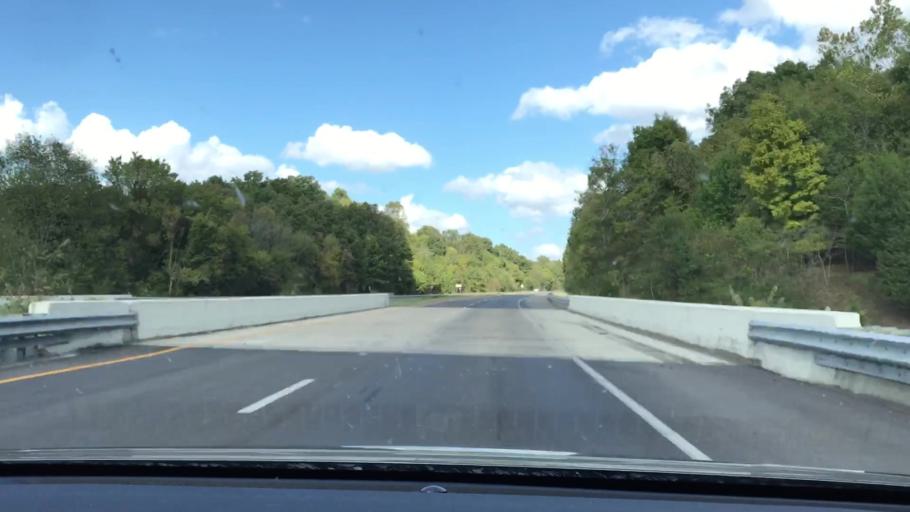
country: US
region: Kentucky
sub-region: Marshall County
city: Benton
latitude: 36.8151
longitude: -88.4867
